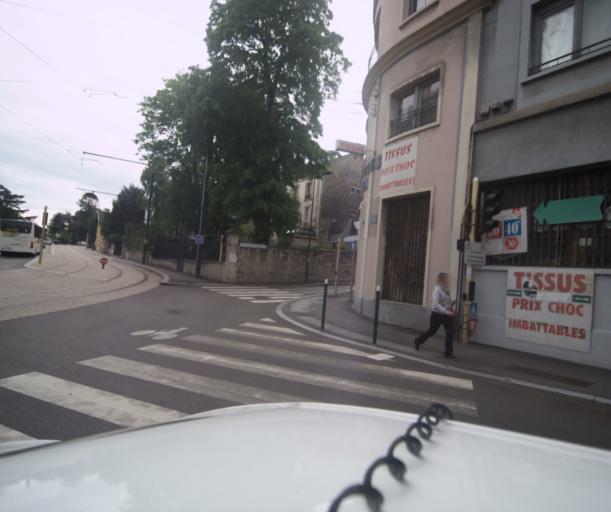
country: FR
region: Franche-Comte
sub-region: Departement du Doubs
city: Besancon
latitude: 47.2464
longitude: 6.0258
